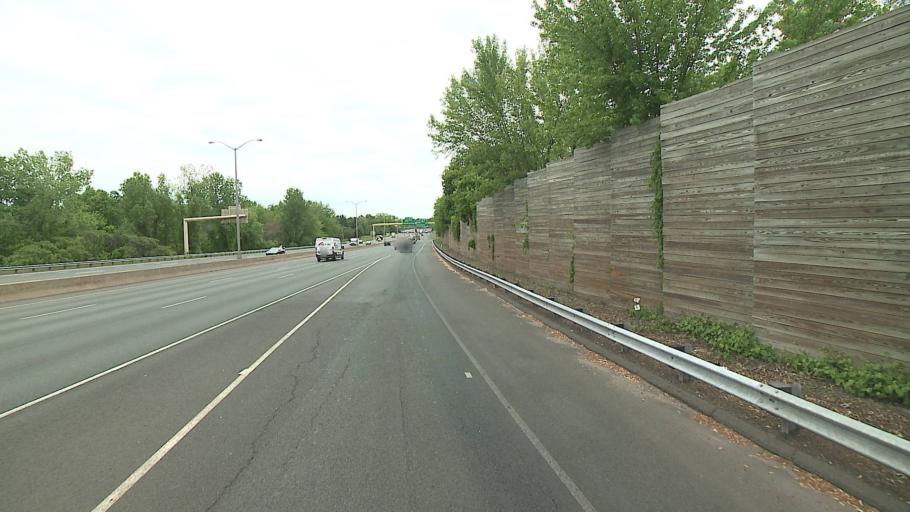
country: US
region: Connecticut
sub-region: Hartford County
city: Thompsonville
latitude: 41.9957
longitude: -72.5866
